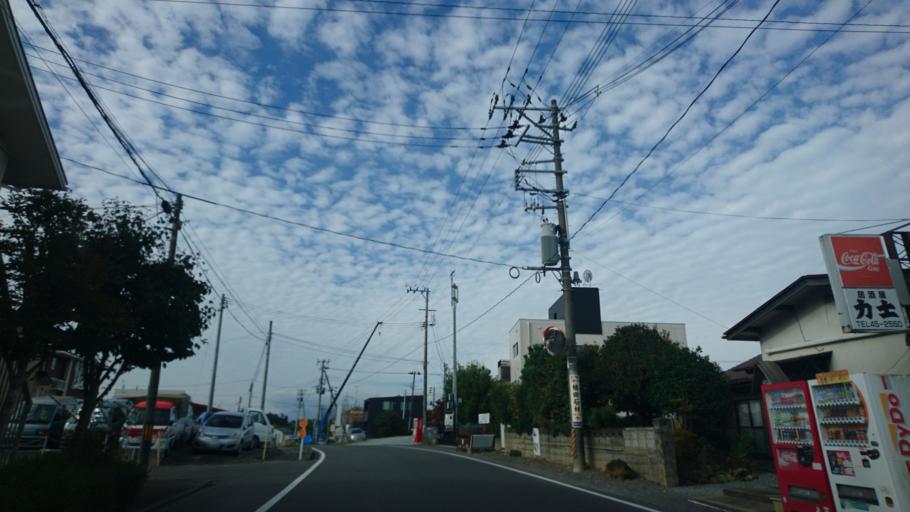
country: JP
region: Fukushima
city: Koriyama
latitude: 37.3498
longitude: 140.3603
